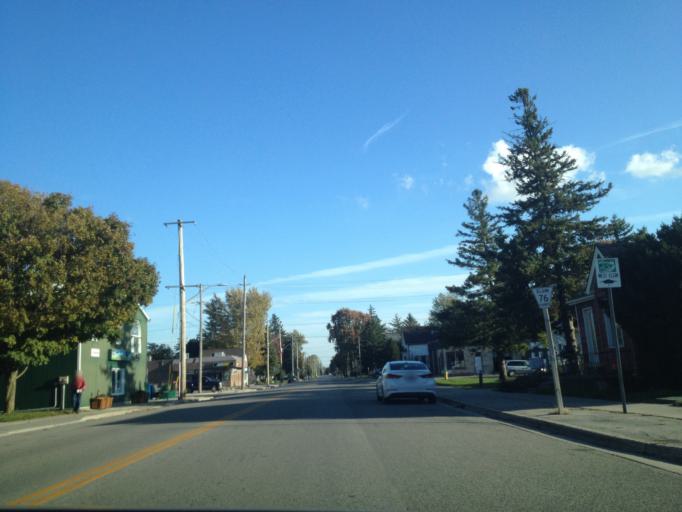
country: CA
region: Ontario
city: Delaware
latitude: 42.6036
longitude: -81.6065
